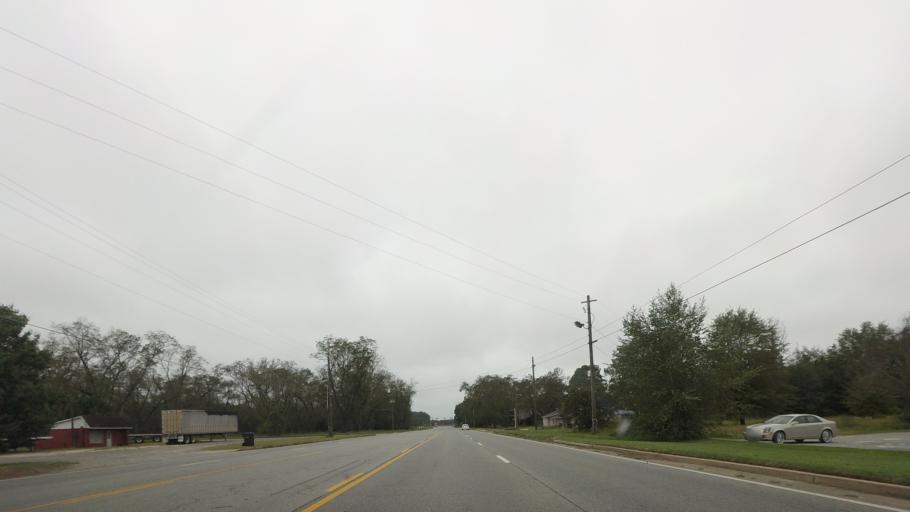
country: US
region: Georgia
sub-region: Berrien County
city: Enigma
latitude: 31.3882
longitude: -83.2273
